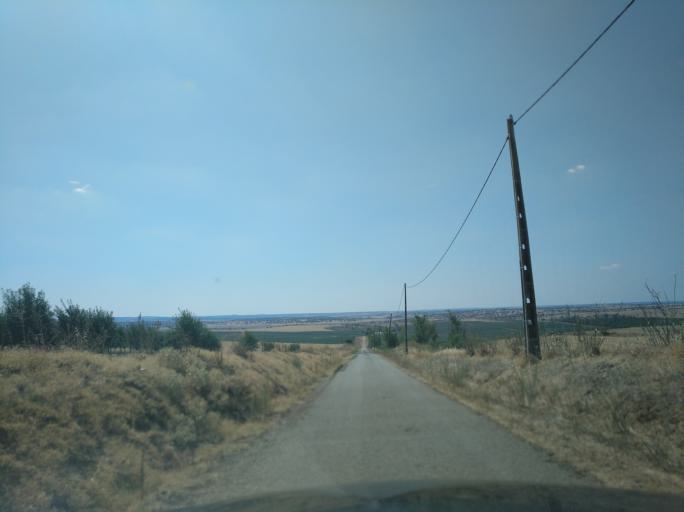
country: PT
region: Portalegre
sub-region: Campo Maior
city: Campo Maior
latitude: 39.0234
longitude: -7.1160
